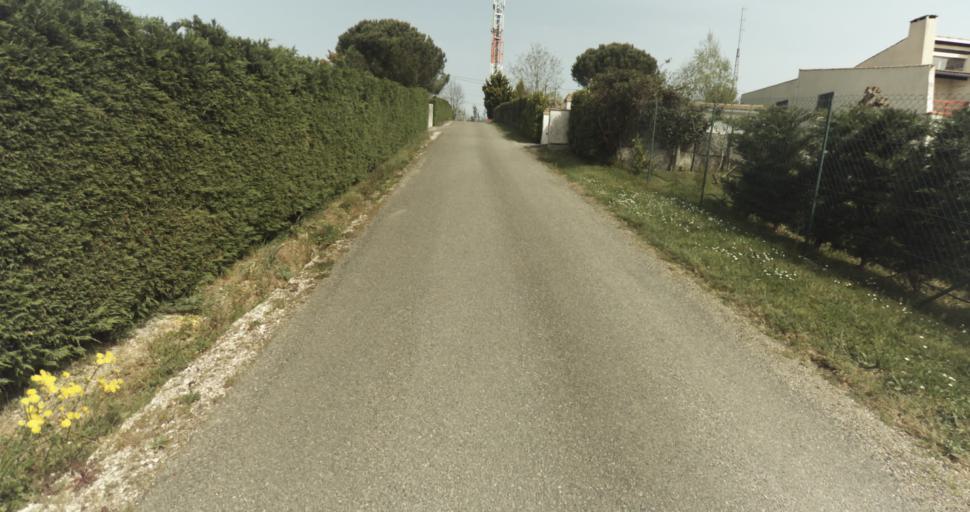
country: FR
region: Midi-Pyrenees
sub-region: Departement du Tarn-et-Garonne
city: Moissac
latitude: 44.1085
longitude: 1.0728
